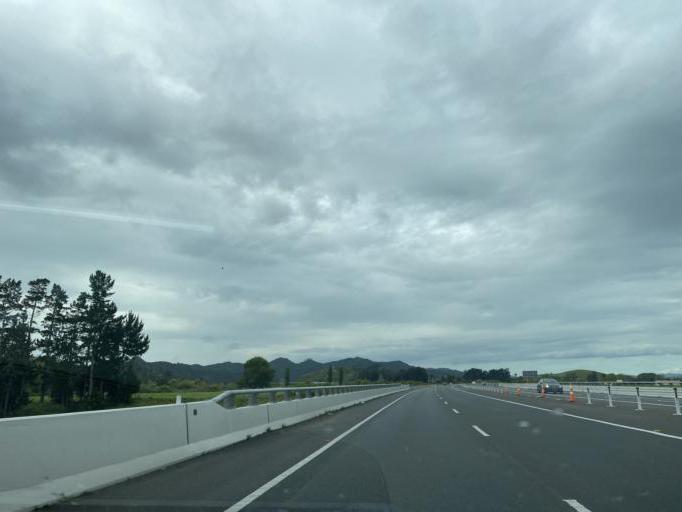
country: NZ
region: Waikato
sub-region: Waikato District
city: Ngaruawahia
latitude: -37.6065
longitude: 175.2049
